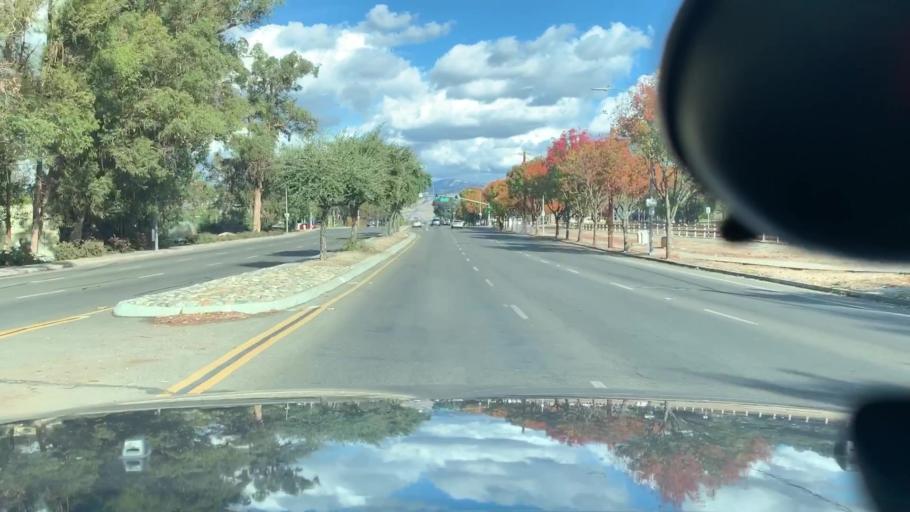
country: US
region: California
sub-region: Santa Clara County
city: Seven Trees
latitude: 37.3105
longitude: -121.8437
